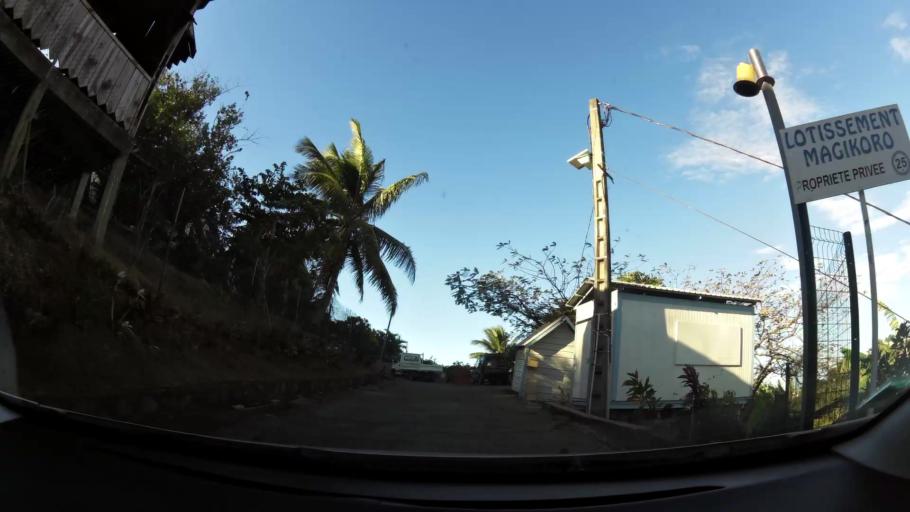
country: YT
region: Koungou
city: Koungou
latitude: -12.7446
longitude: 45.2168
